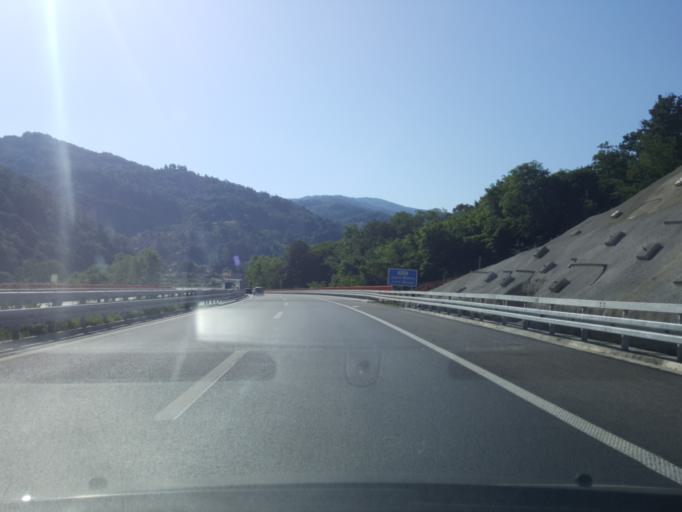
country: RS
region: Central Serbia
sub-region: Jablanicki Okrug
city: Vlasotince
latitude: 42.8650
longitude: 22.1104
